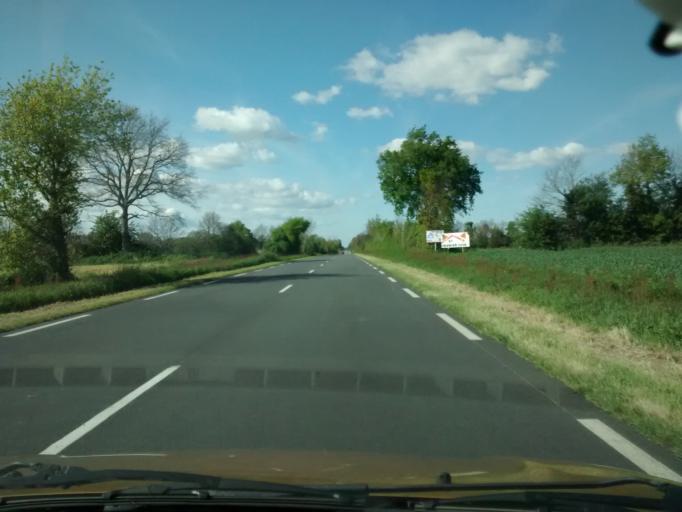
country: FR
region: Pays de la Loire
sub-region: Departement de la Loire-Atlantique
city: Geneston
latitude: 47.0293
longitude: -1.5057
